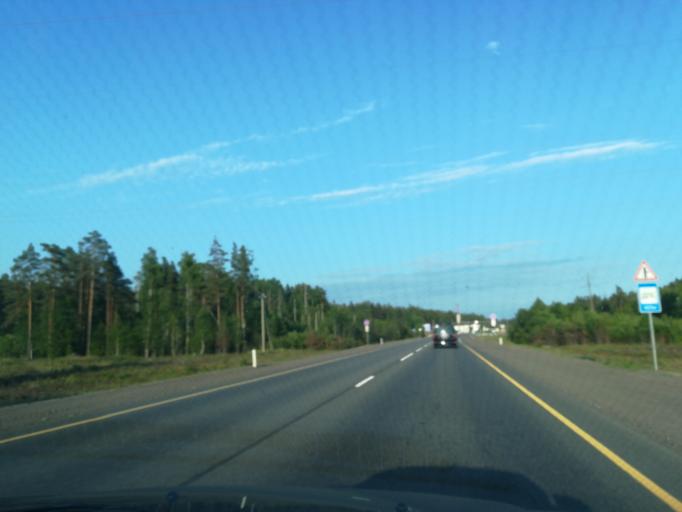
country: RU
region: Leningrad
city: Vyborg
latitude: 60.6658
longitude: 28.9239
